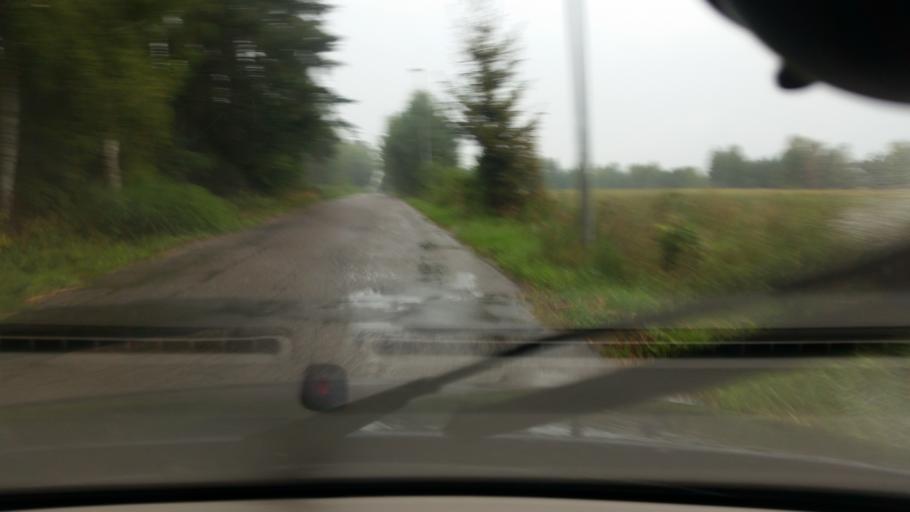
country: PL
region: Pomeranian Voivodeship
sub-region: Powiat wejherowski
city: Choczewo
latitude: 54.7645
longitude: 17.7930
